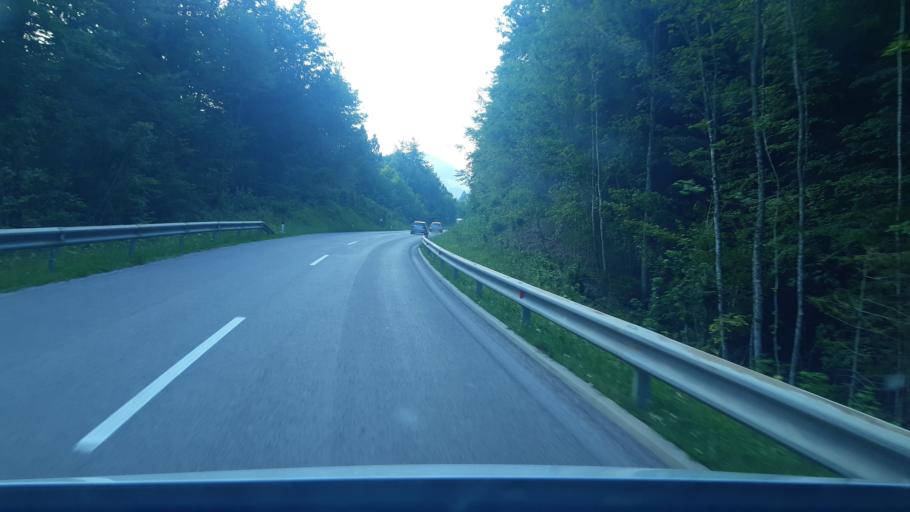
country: SI
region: Semic
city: Semic
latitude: 45.6580
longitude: 15.1168
